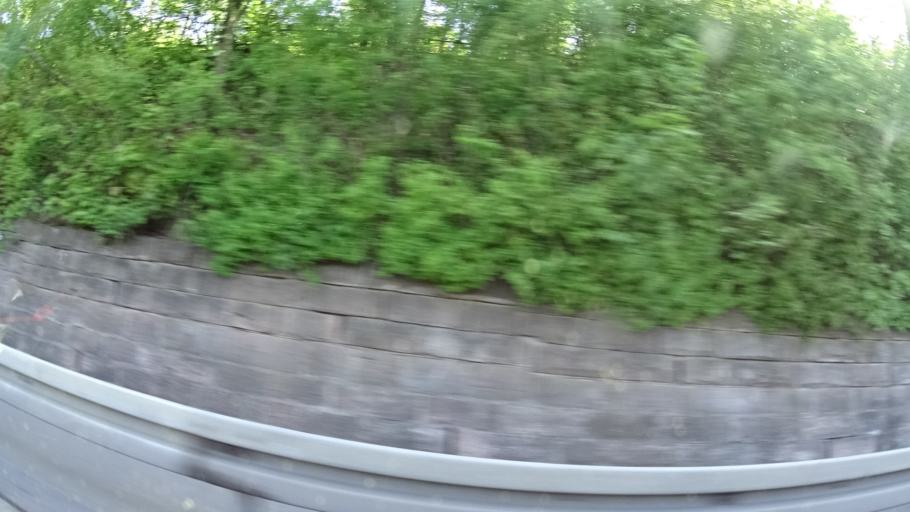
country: DE
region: Baden-Wuerttemberg
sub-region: Karlsruhe Region
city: Rohrdorf
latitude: 48.5681
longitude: 8.6982
